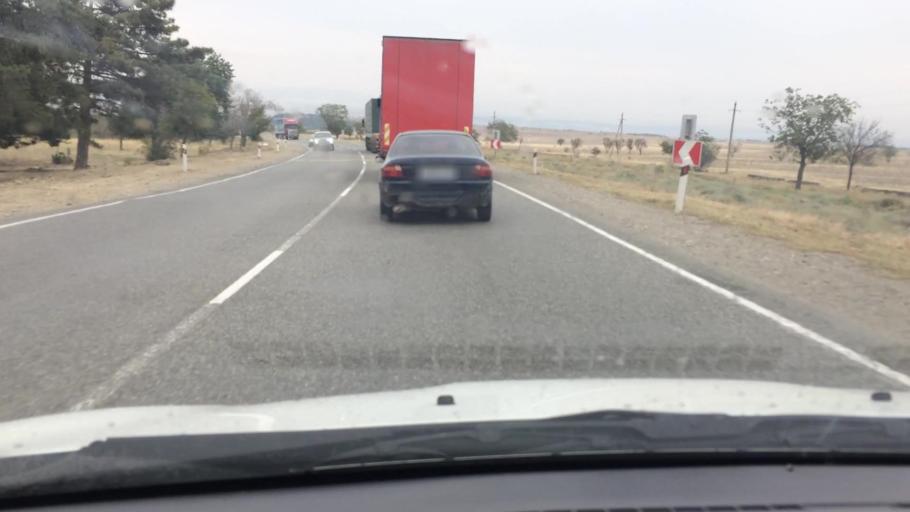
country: GE
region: T'bilisi
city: Tbilisi
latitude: 41.6386
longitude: 44.8744
